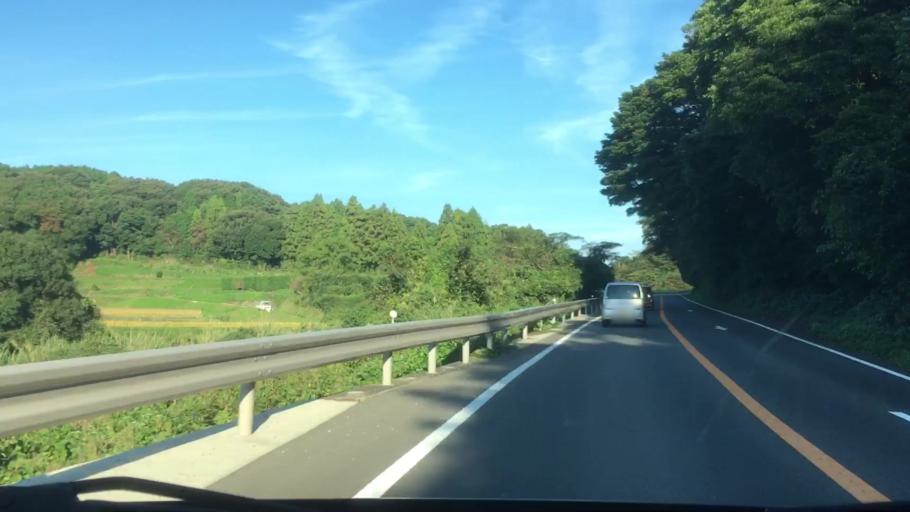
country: JP
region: Nagasaki
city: Sasebo
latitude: 33.0405
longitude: 129.6899
